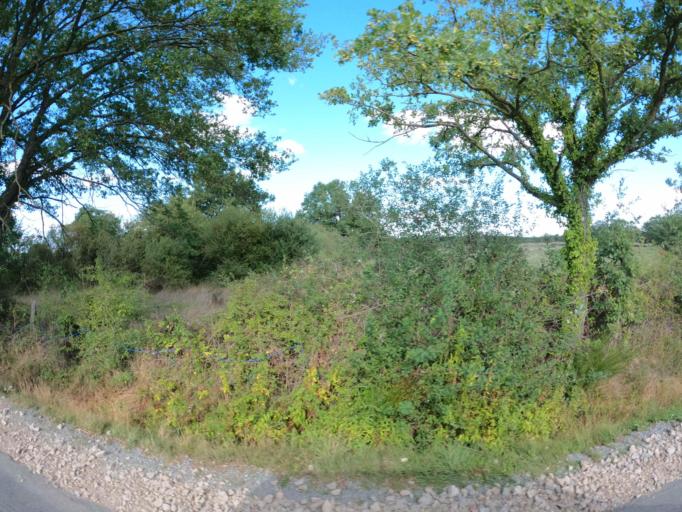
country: FR
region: Auvergne
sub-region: Departement de l'Allier
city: Doyet
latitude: 46.3884
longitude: 2.7649
